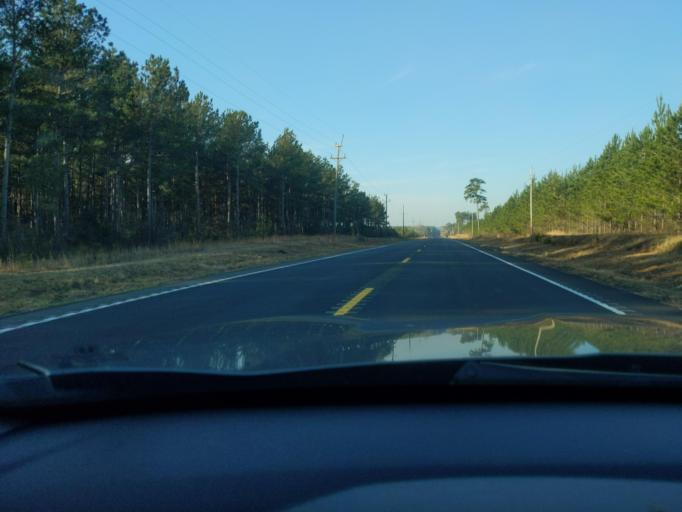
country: US
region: South Carolina
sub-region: Greenwood County
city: Ninety Six
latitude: 34.2041
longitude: -81.8213
